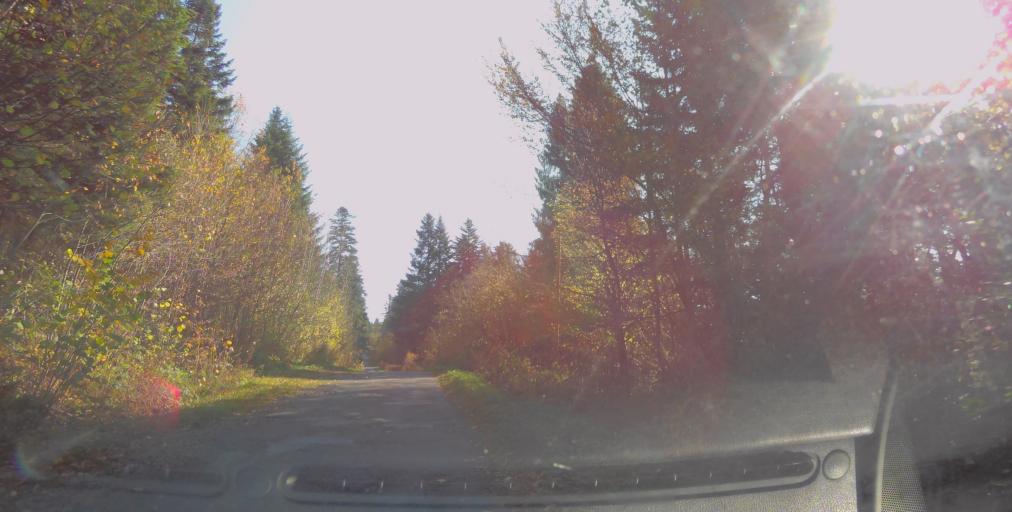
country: PL
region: Subcarpathian Voivodeship
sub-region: Powiat leski
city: Polanczyk
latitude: 49.3234
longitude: 22.4341
